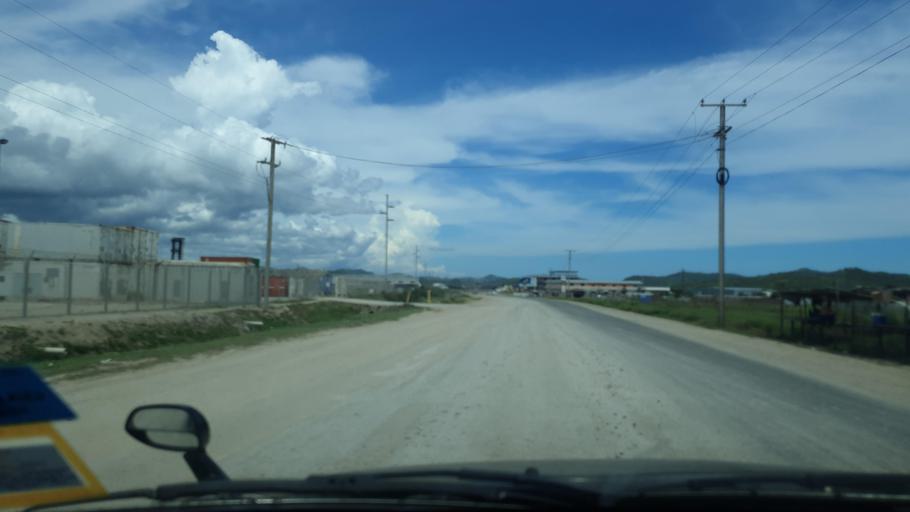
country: PG
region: National Capital
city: Port Moresby
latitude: -9.4172
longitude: 147.0755
